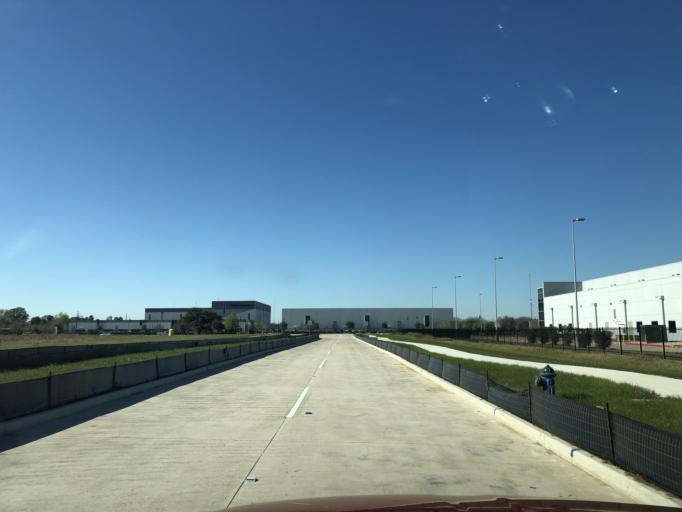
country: US
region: Texas
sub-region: Fort Bend County
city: Fresno
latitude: 29.5890
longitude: -95.3984
